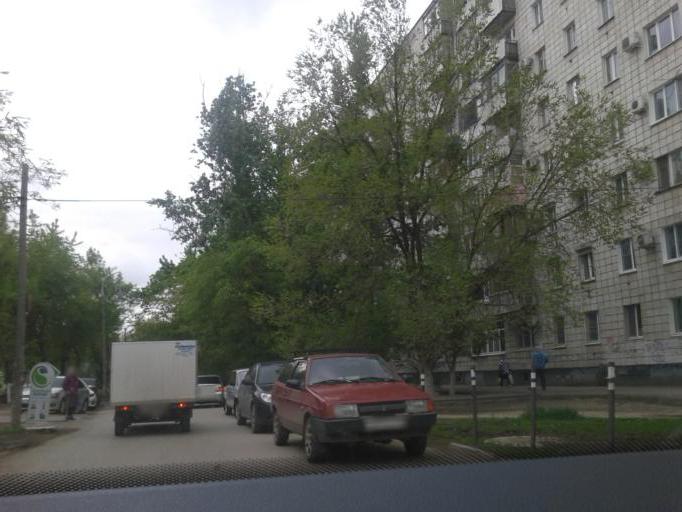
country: RU
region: Volgograd
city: Volgograd
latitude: 48.6075
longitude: 44.4216
